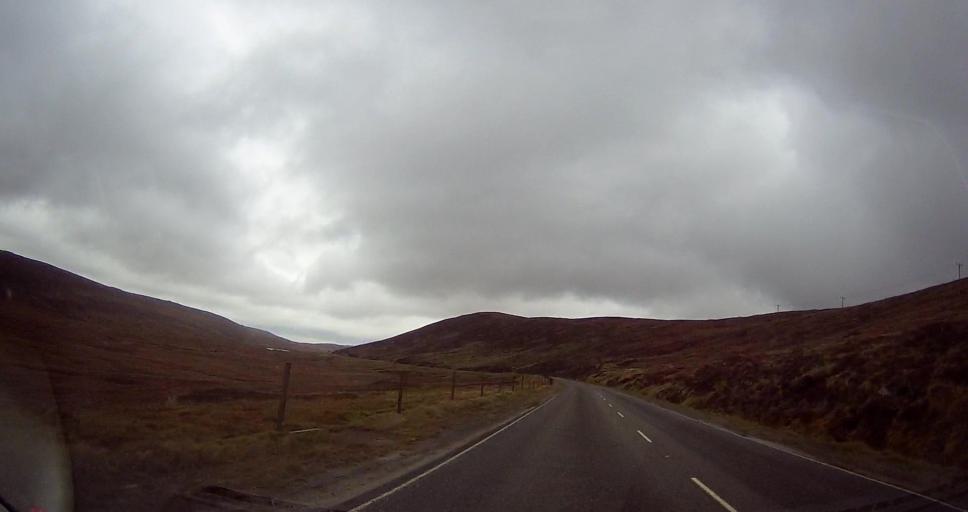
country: GB
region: Scotland
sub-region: Shetland Islands
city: Lerwick
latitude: 60.2995
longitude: -1.2391
